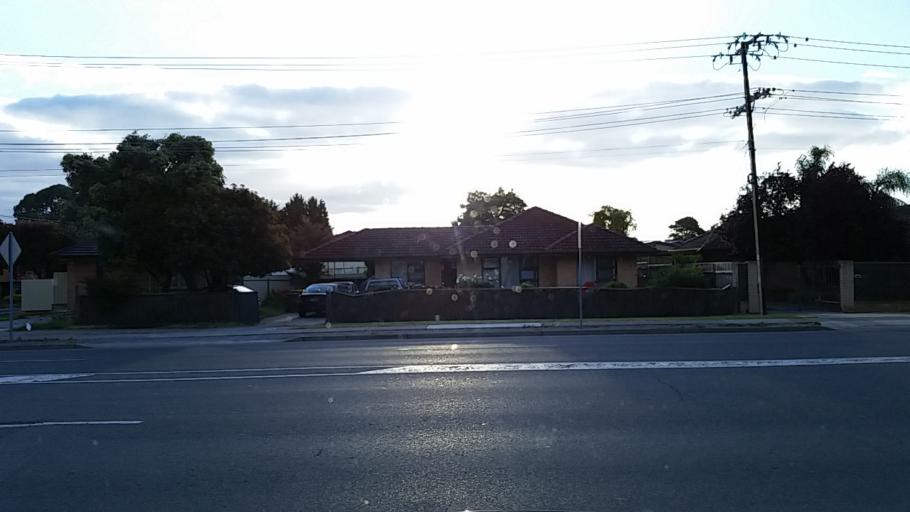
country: AU
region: South Australia
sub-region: Tea Tree Gully
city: Modbury
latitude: -34.8300
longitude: 138.6879
